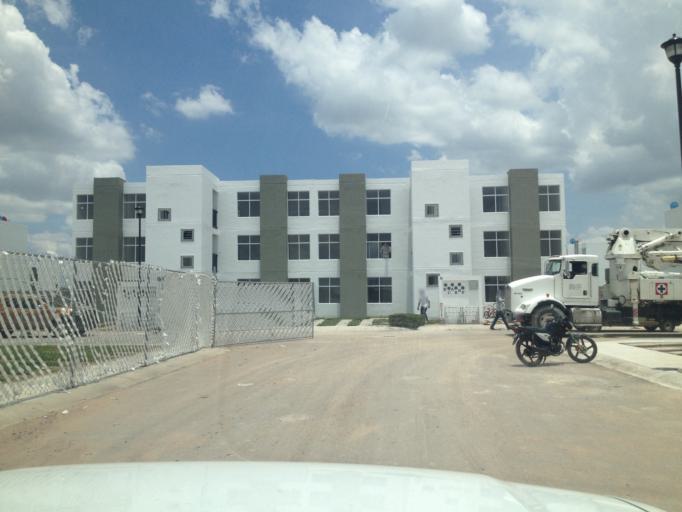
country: MX
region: Aguascalientes
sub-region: Aguascalientes
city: San Sebastian [Fraccionamiento]
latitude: 21.8043
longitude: -102.2760
